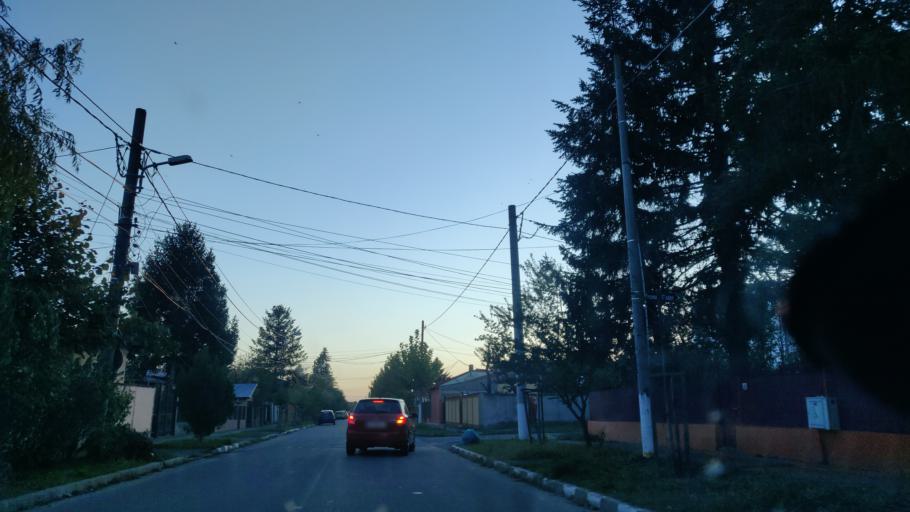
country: RO
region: Ilfov
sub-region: Comuna Chitila
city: Rudeni
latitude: 44.4694
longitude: 25.9967
